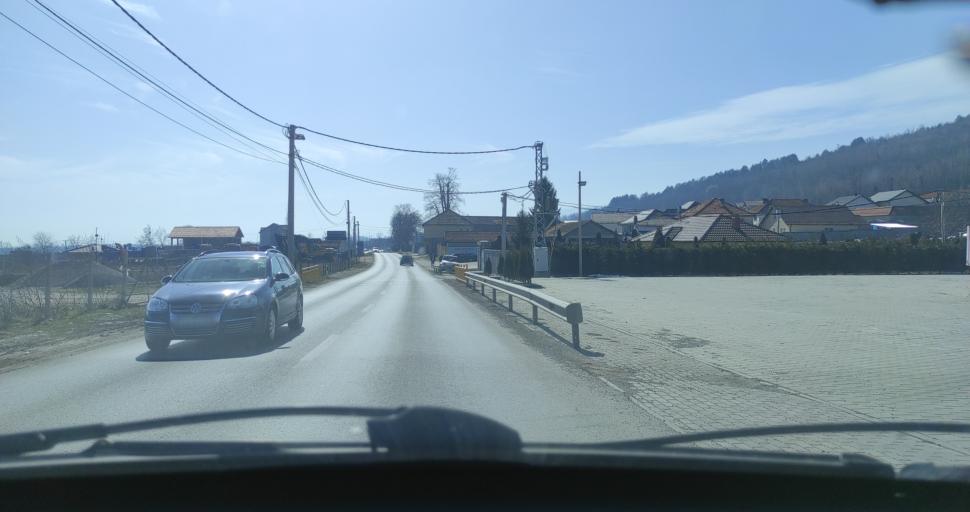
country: XK
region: Gjakova
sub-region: Komuna e Decanit
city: Lebushe
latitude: 42.5703
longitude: 20.2931
